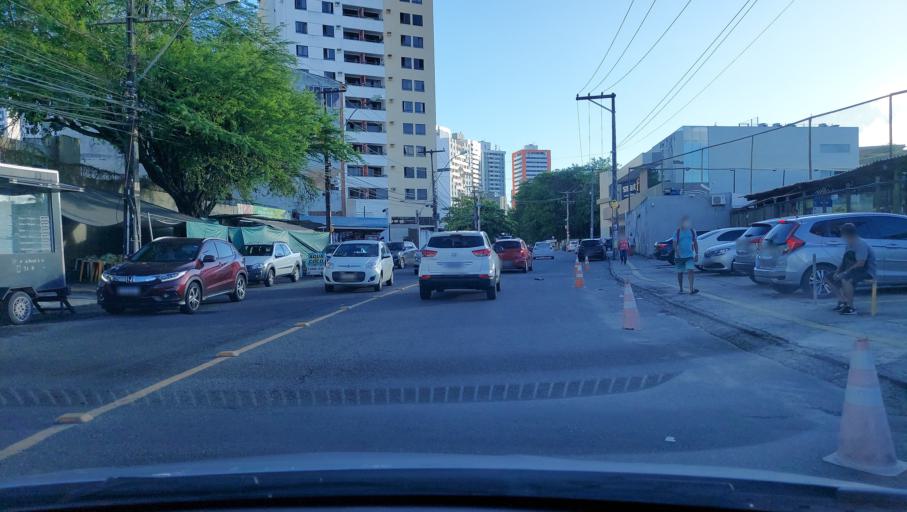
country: BR
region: Bahia
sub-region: Salvador
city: Salvador
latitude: -12.9708
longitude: -38.4388
